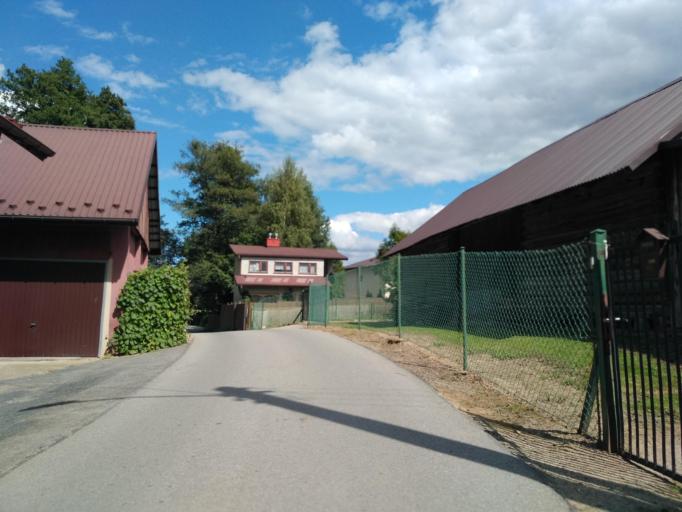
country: PL
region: Subcarpathian Voivodeship
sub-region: Powiat jasielski
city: Jaslo
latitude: 49.7585
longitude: 21.5018
